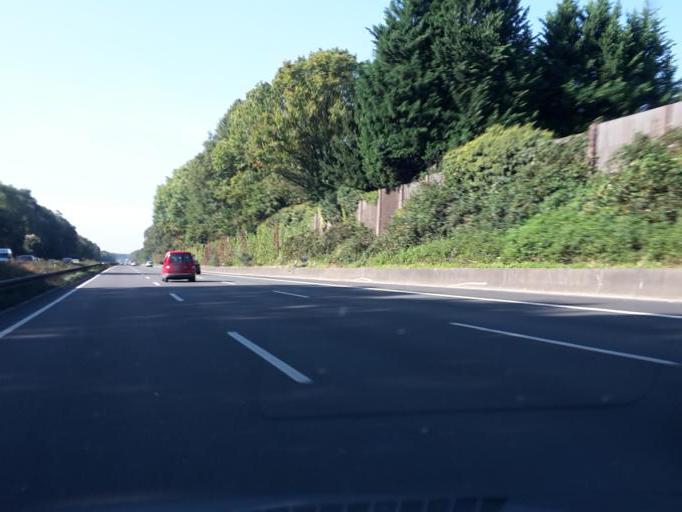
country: DE
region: North Rhine-Westphalia
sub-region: Regierungsbezirk Koln
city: Rosrath
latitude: 50.8956
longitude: 7.1636
